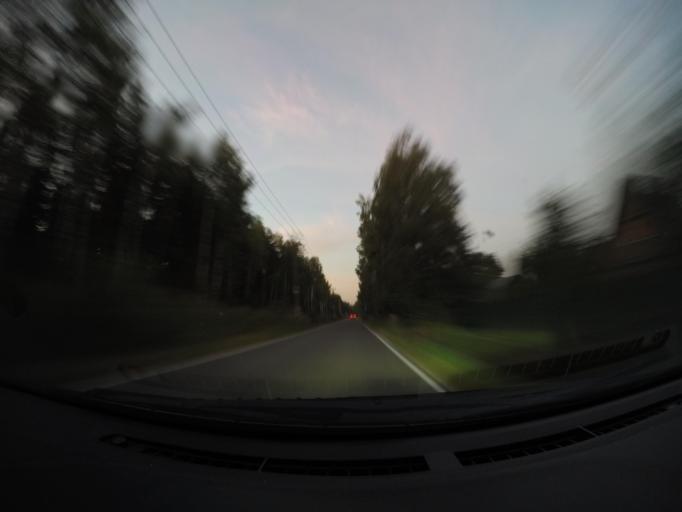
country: RU
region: Moskovskaya
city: Rechitsy
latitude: 55.5458
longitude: 38.4490
